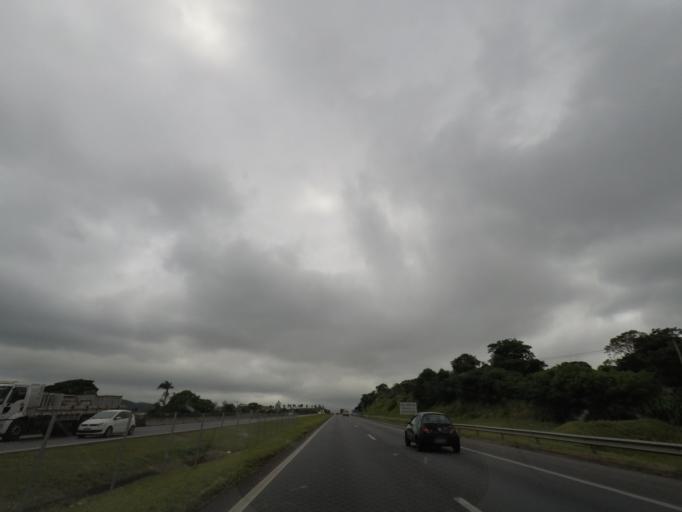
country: BR
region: Sao Paulo
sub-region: Atibaia
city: Atibaia
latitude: -23.1078
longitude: -46.5049
